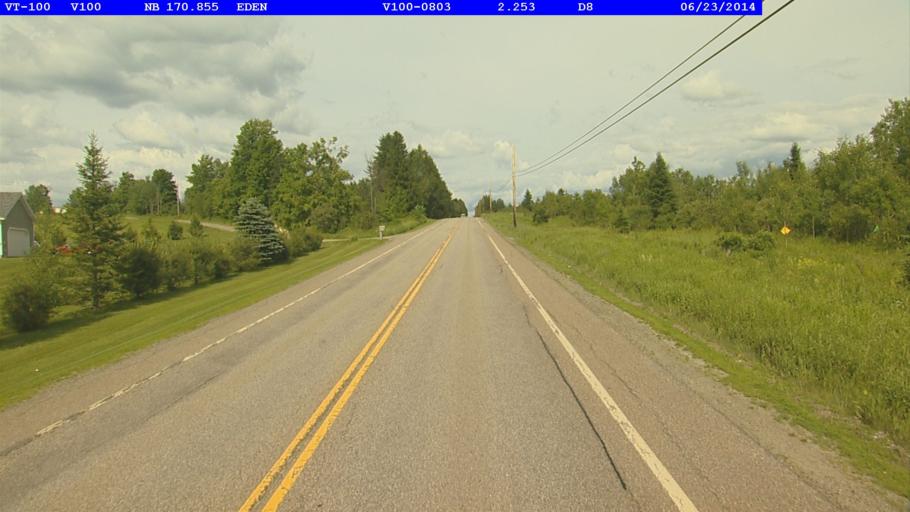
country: US
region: Vermont
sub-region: Lamoille County
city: Hyde Park
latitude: 44.7038
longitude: -72.5576
